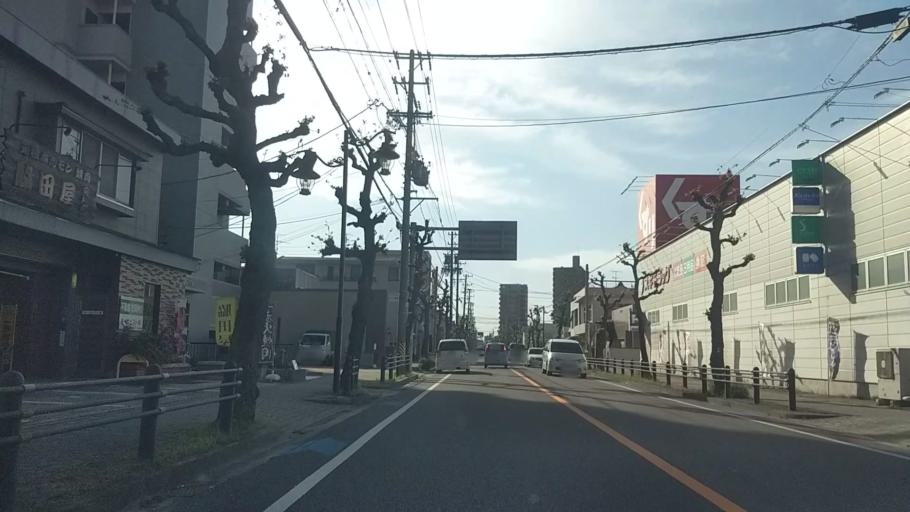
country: JP
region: Aichi
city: Anjo
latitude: 34.9605
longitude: 137.0821
